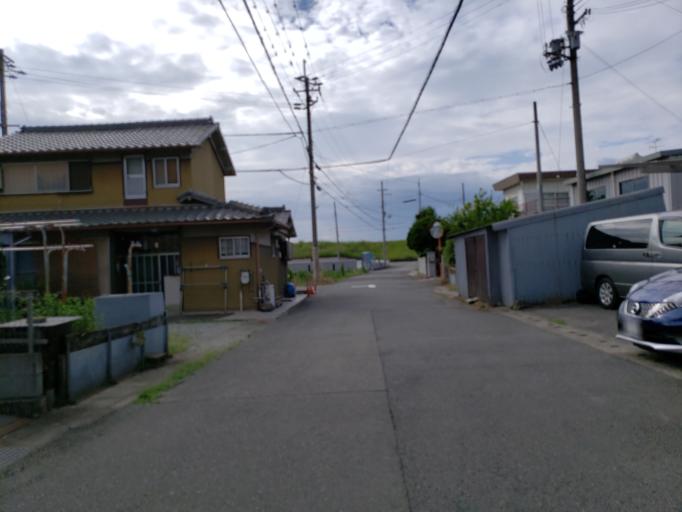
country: JP
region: Hyogo
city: Kakogawacho-honmachi
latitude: 34.7693
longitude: 134.8238
